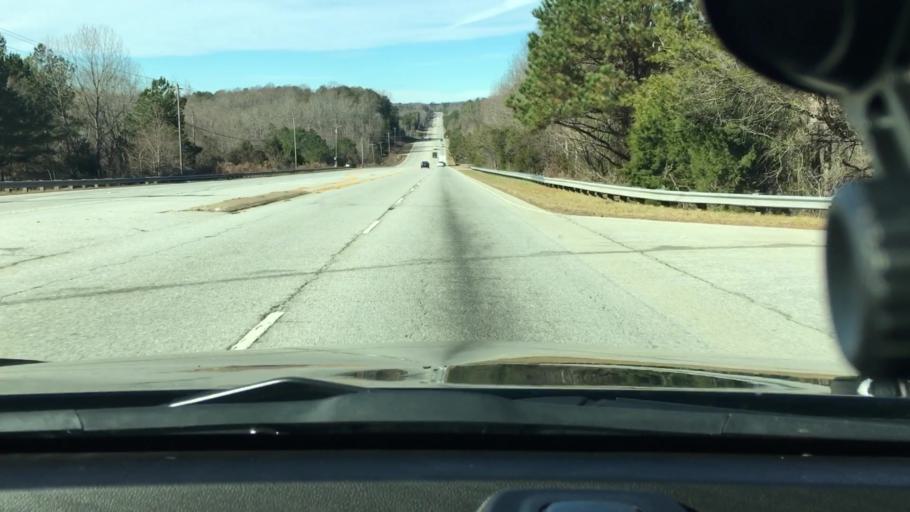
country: US
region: South Carolina
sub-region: Spartanburg County
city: Pacolet
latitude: 34.9099
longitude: -81.8027
